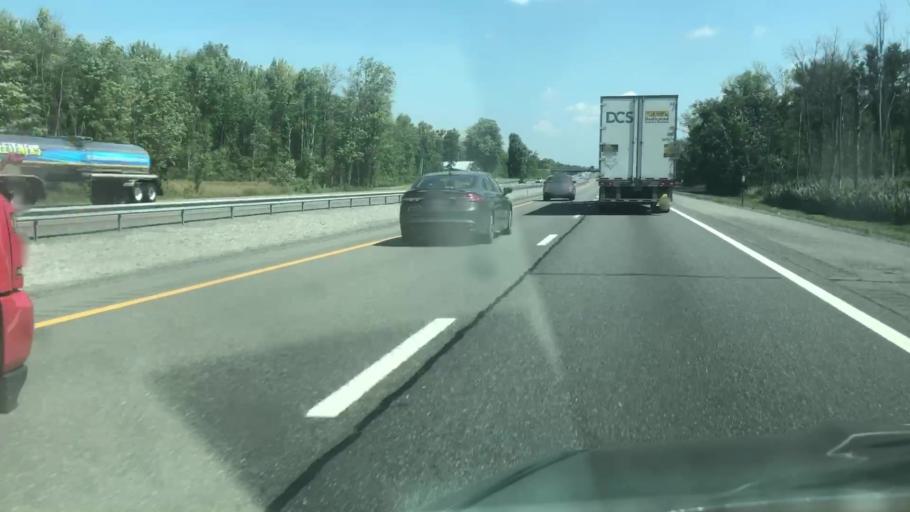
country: US
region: New York
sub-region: Madison County
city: Oneida
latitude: 43.1082
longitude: -75.6721
